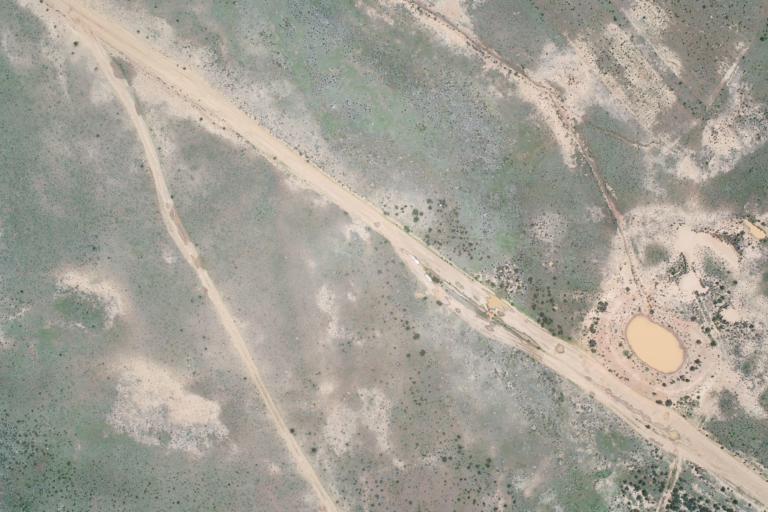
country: BO
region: La Paz
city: Curahuara de Carangas
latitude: -17.2854
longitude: -68.5141
